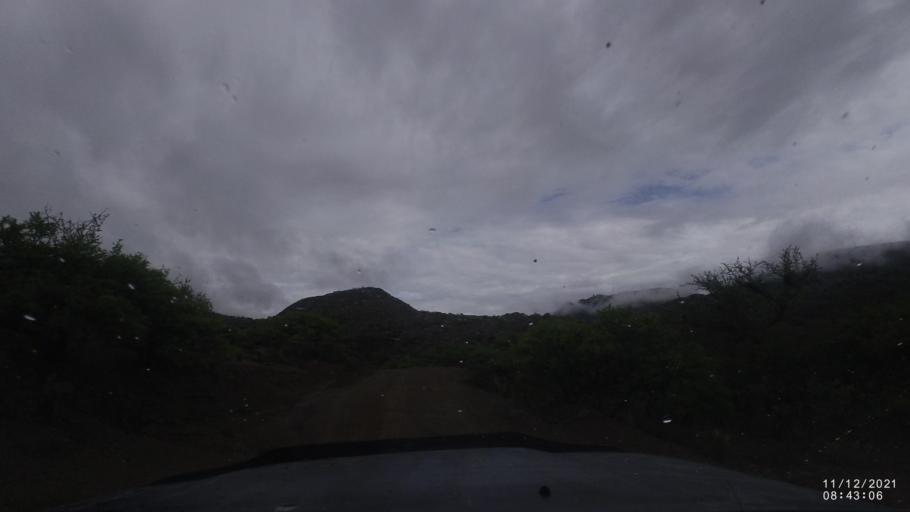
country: BO
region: Cochabamba
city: Tarata
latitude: -17.9143
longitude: -65.9361
